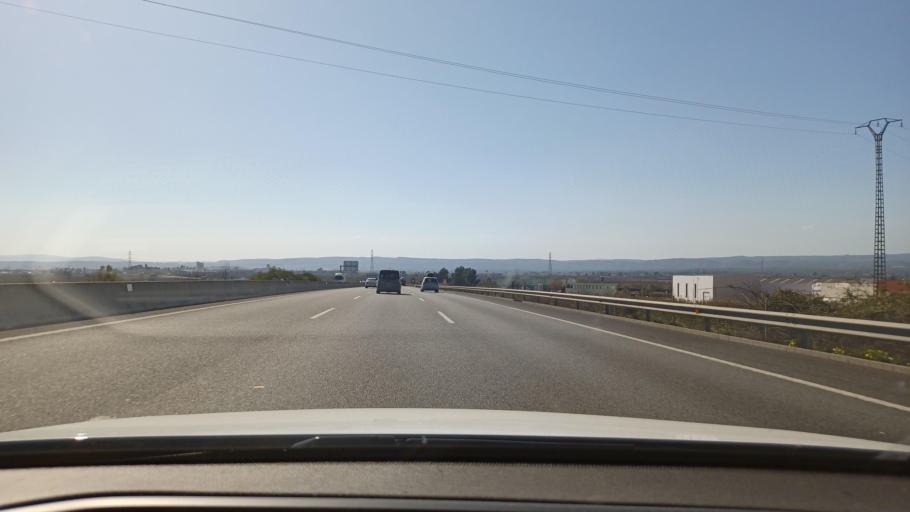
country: ES
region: Valencia
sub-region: Provincia de Valencia
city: L'Alcudia
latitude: 39.1851
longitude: -0.5065
